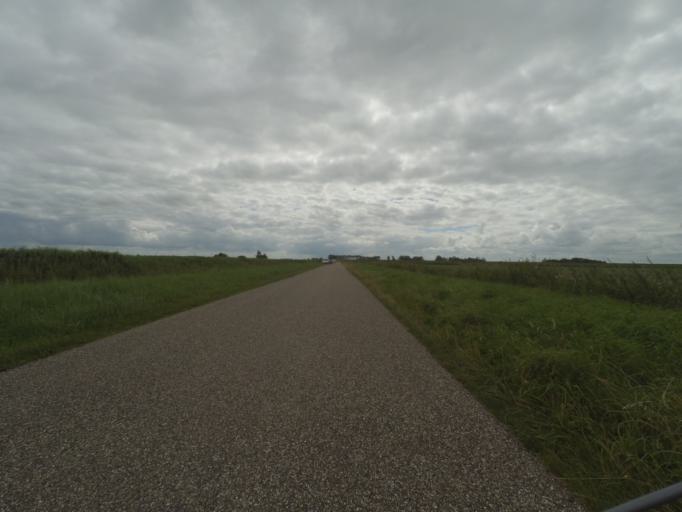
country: NL
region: Friesland
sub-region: Gemeente Dongeradeel
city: Anjum
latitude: 53.3453
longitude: 6.1530
